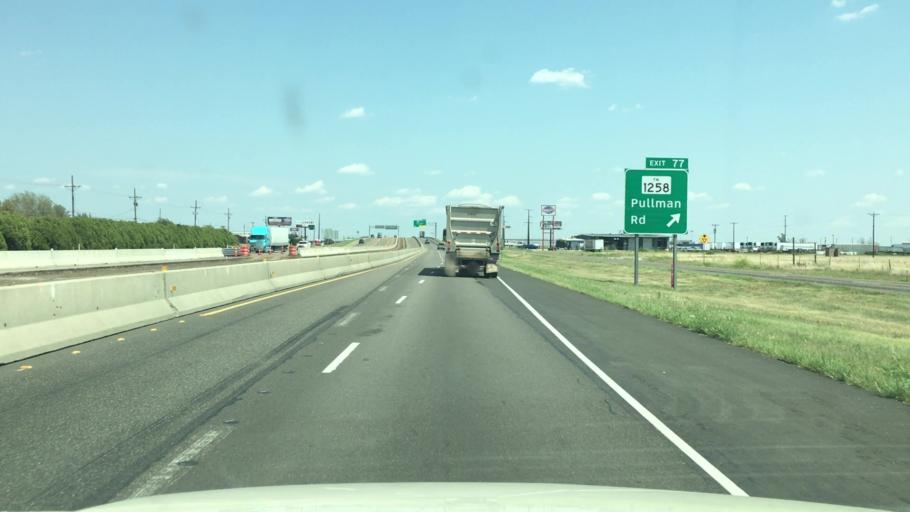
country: US
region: Texas
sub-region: Potter County
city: Amarillo
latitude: 35.1927
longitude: -101.7134
